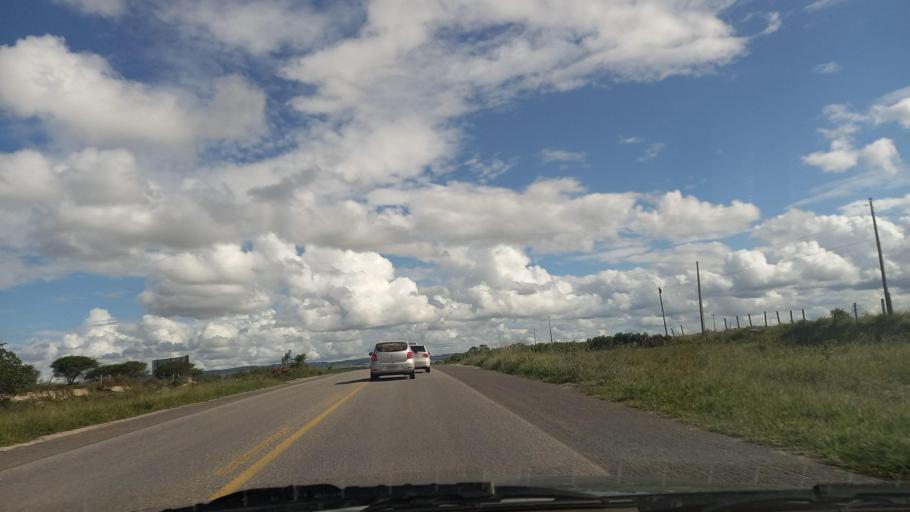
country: BR
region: Pernambuco
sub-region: Sao Joao
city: Sao Joao
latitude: -8.7856
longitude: -36.4324
